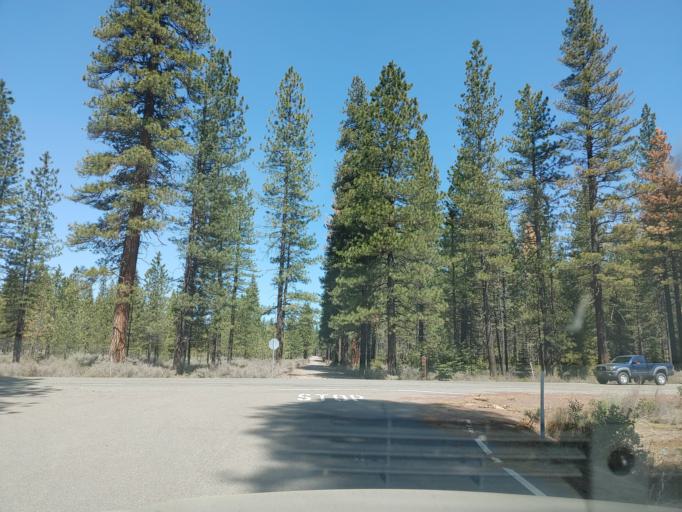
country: US
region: California
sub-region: Siskiyou County
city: McCloud
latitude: 41.2635
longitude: -121.9426
